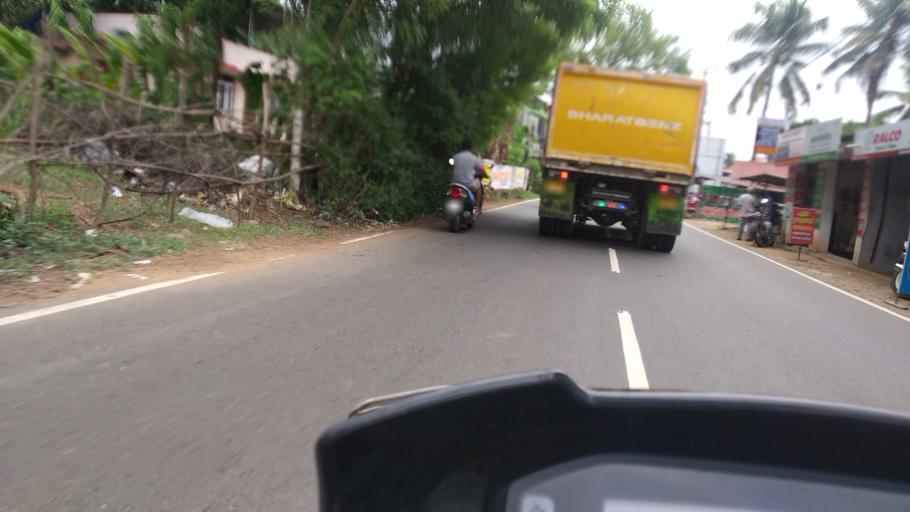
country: IN
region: Kerala
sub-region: Ernakulam
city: Aluva
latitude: 10.1549
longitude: 76.2943
